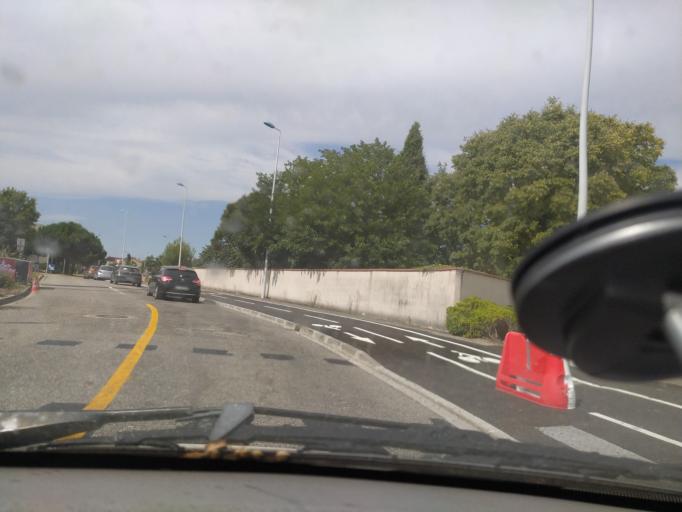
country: FR
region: Midi-Pyrenees
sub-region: Departement de la Haute-Garonne
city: Colomiers
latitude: 43.6042
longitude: 1.3360
